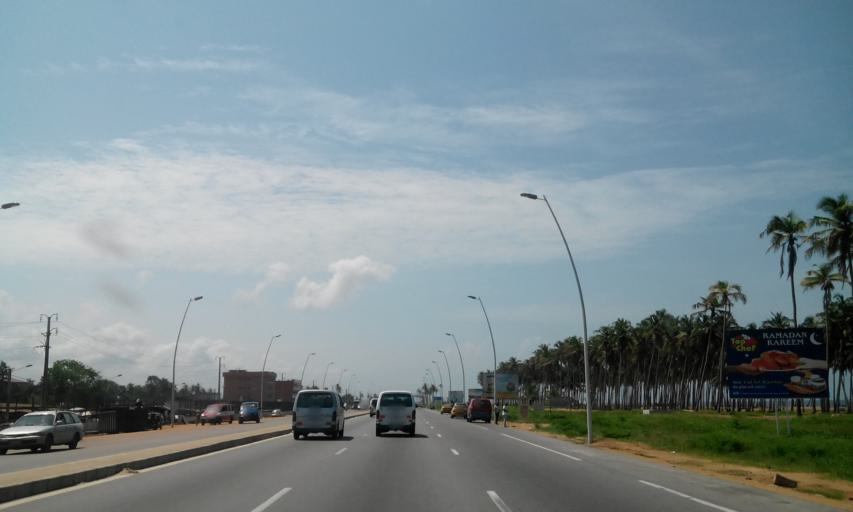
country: CI
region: Lagunes
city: Bingerville
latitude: 5.2380
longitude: -3.8880
